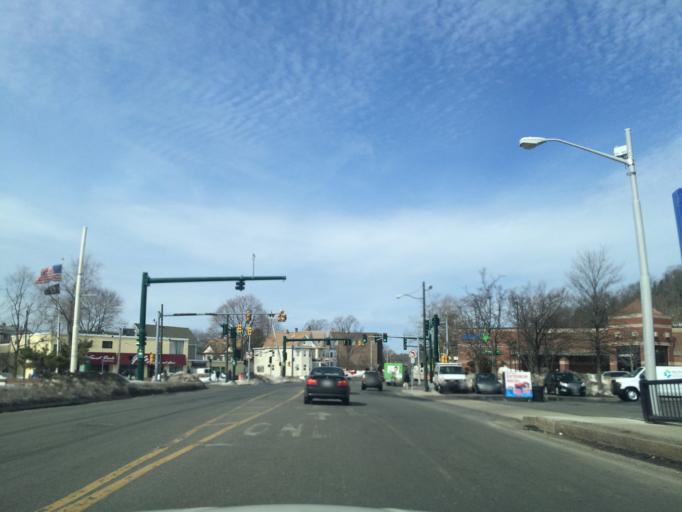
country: US
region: Massachusetts
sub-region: Middlesex County
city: Belmont
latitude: 42.3877
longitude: -71.1903
